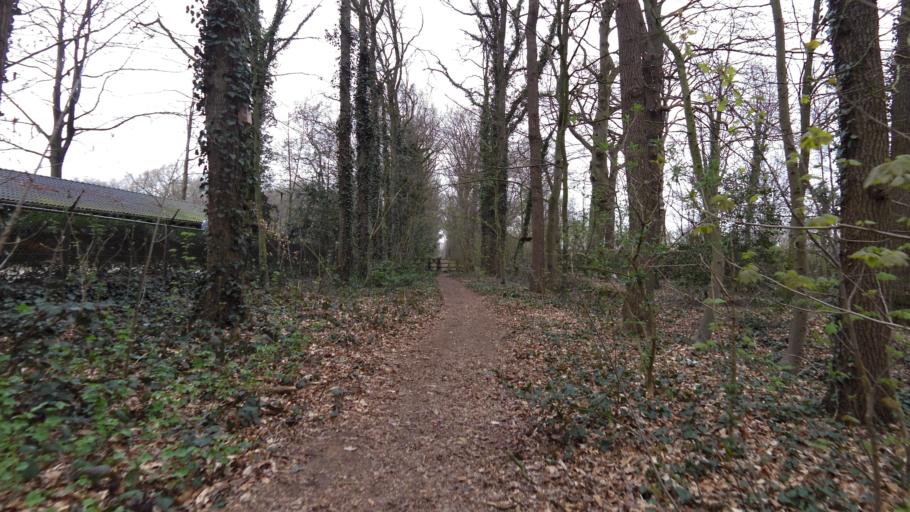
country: NL
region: Gelderland
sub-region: Gemeente Barneveld
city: Zwartebroek
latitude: 52.2057
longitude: 5.5131
